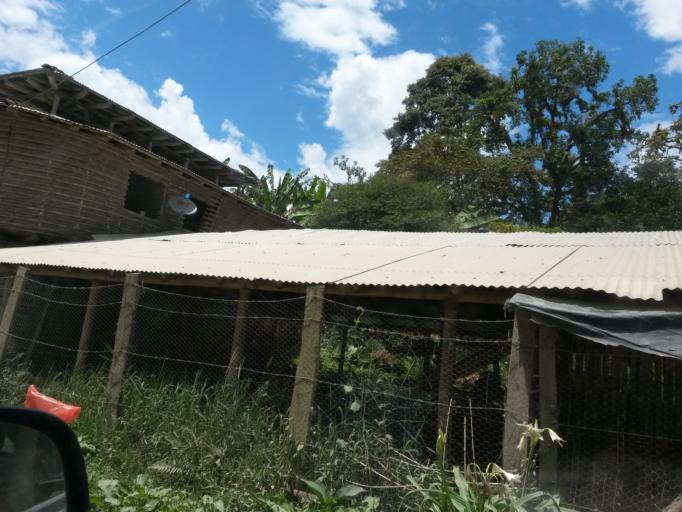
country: CO
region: Cauca
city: Inza
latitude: 2.5531
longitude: -76.0522
